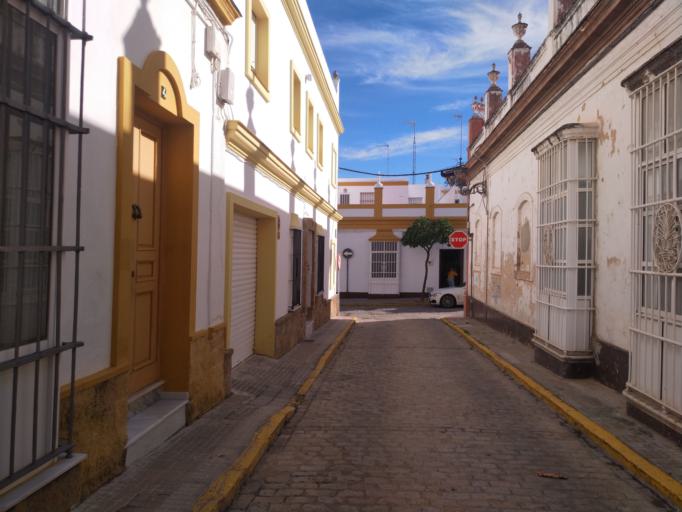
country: ES
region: Andalusia
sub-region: Provincia de Cadiz
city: San Fernando
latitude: 36.4689
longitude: -6.1949
